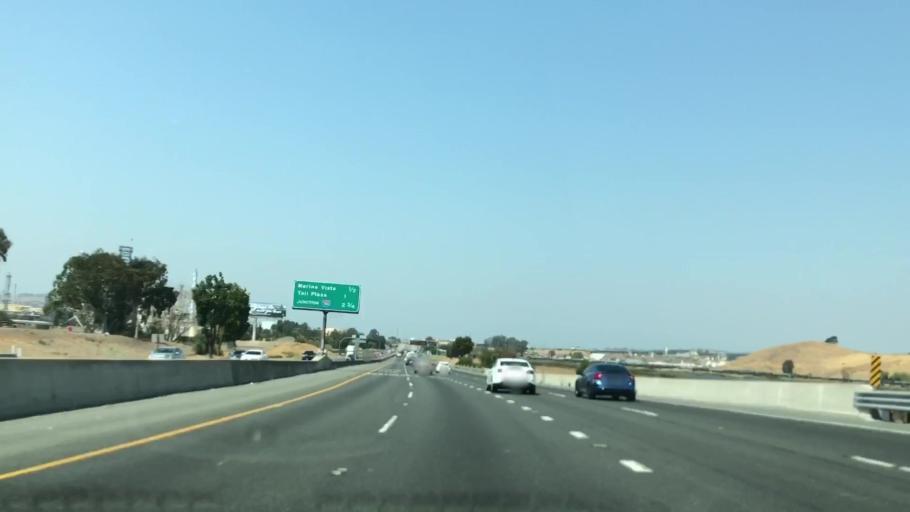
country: US
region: California
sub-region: Contra Costa County
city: Vine Hill
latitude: 38.0196
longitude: -122.0975
